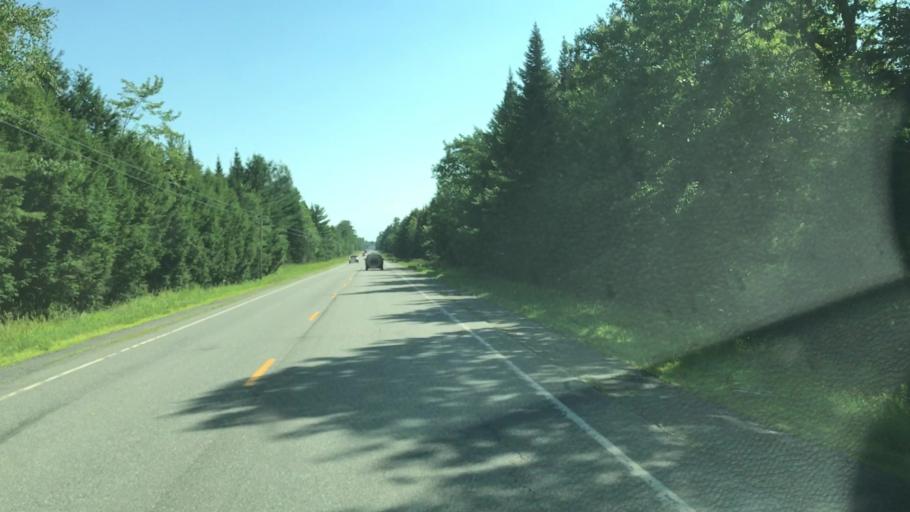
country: US
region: Maine
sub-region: Penobscot County
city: Enfield
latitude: 45.3113
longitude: -68.6074
